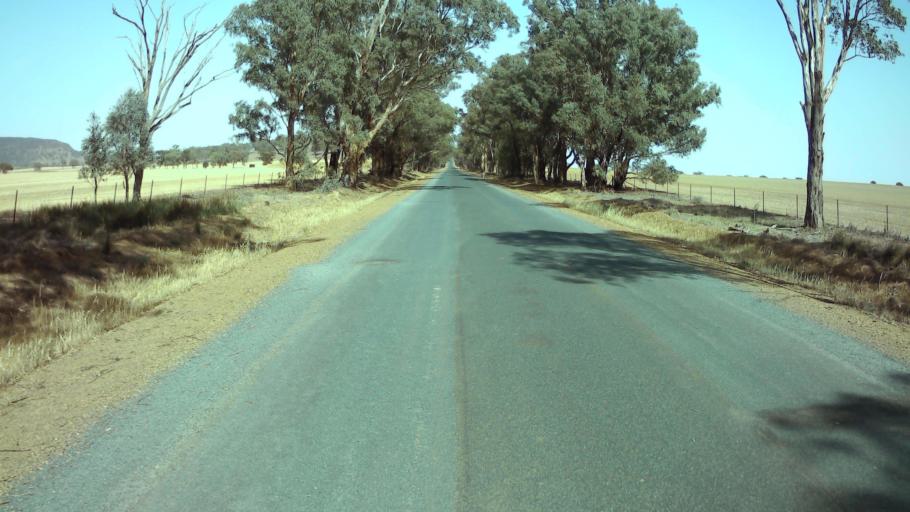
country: AU
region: New South Wales
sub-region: Weddin
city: Grenfell
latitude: -33.8633
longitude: 148.0309
